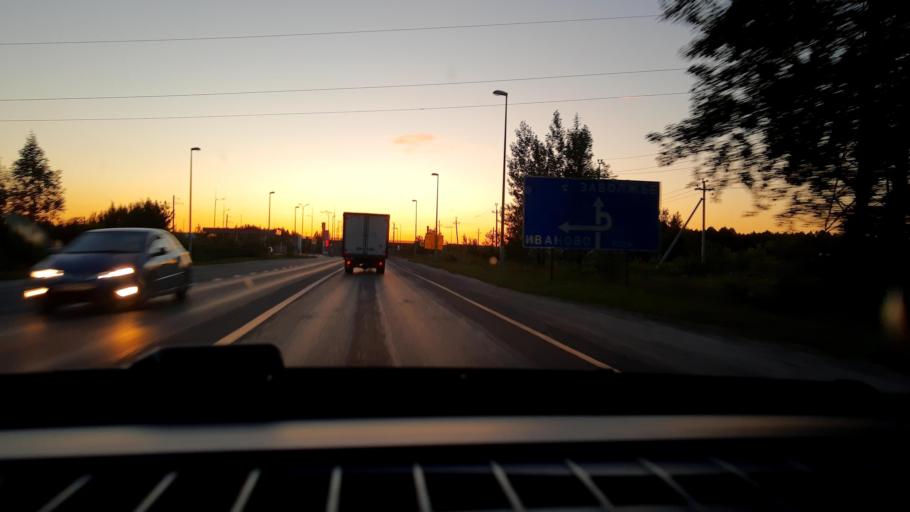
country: RU
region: Nizjnij Novgorod
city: Zavolzh'ye
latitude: 56.6148
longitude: 43.4364
